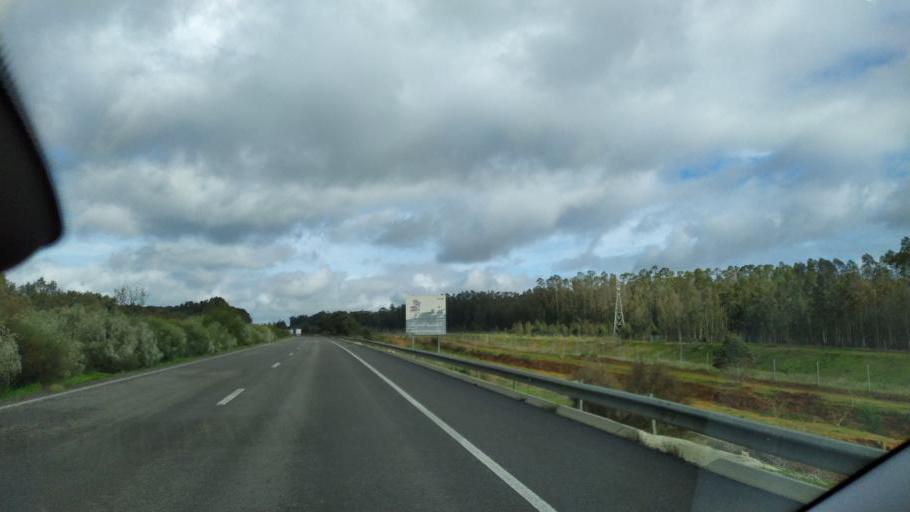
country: MA
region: Gharb-Chrarda-Beni Hssen
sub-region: Kenitra Province
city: Lalla Mimouna
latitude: 34.9189
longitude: -6.2043
